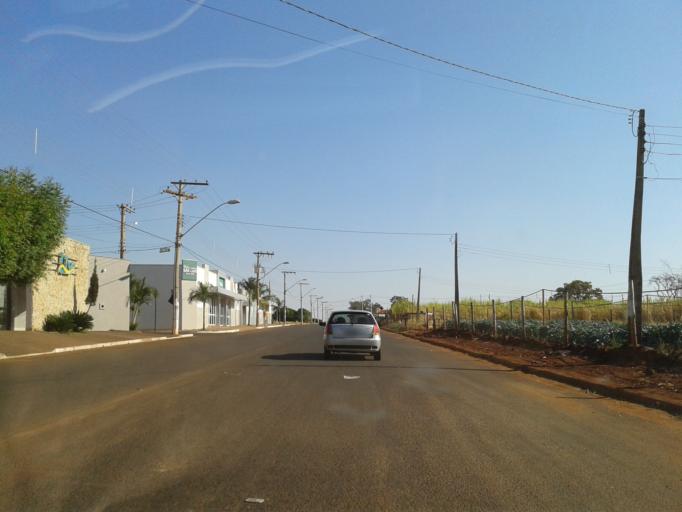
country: BR
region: Minas Gerais
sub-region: Ituiutaba
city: Ituiutaba
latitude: -18.9876
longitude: -49.4848
